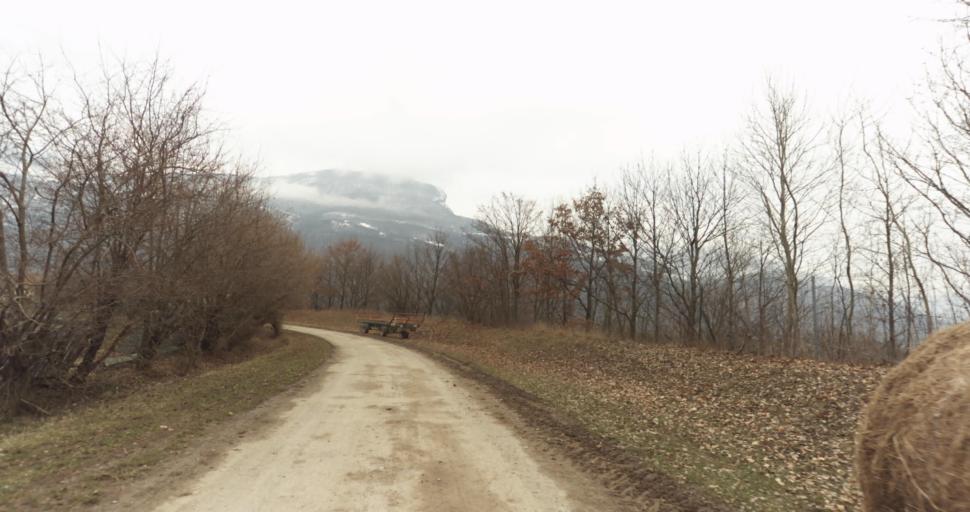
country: FR
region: Rhone-Alpes
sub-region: Departement de l'Isere
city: Vif
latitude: 45.0436
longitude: 5.6764
